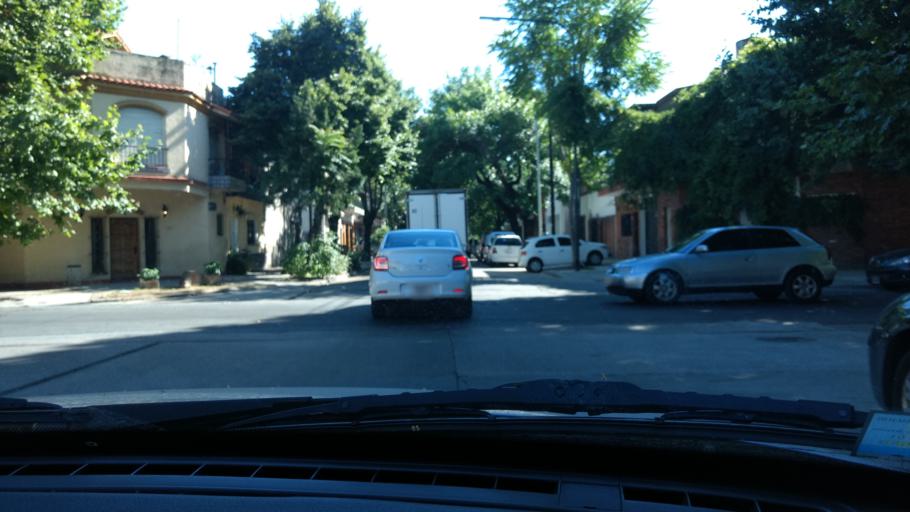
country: AR
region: Buenos Aires F.D.
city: Villa Santa Rita
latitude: -34.6186
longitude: -58.5166
